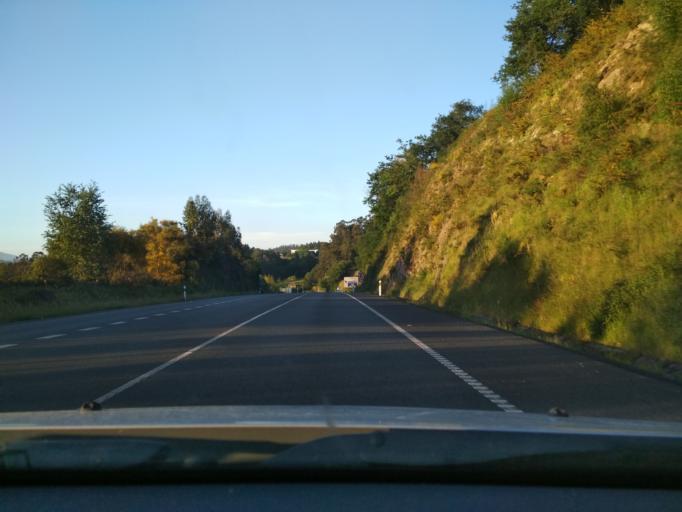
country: ES
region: Galicia
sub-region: Provincia de Pontevedra
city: Barro
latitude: 42.5165
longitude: -8.6413
